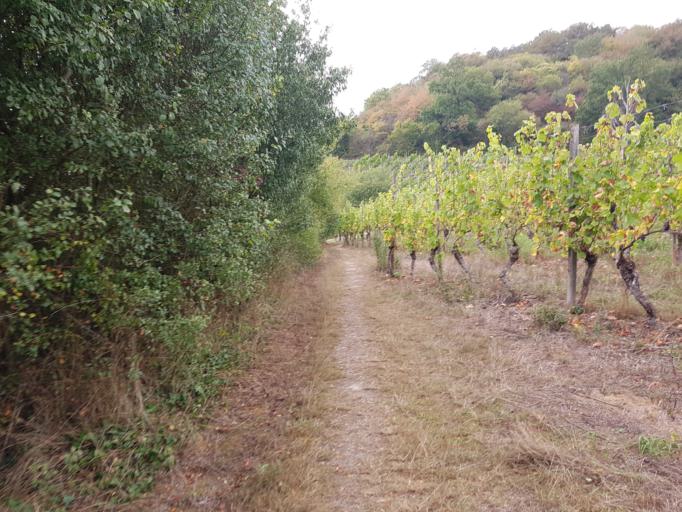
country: DE
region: Rheinland-Pfalz
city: Bacharach
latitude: 50.0617
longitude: 7.7641
